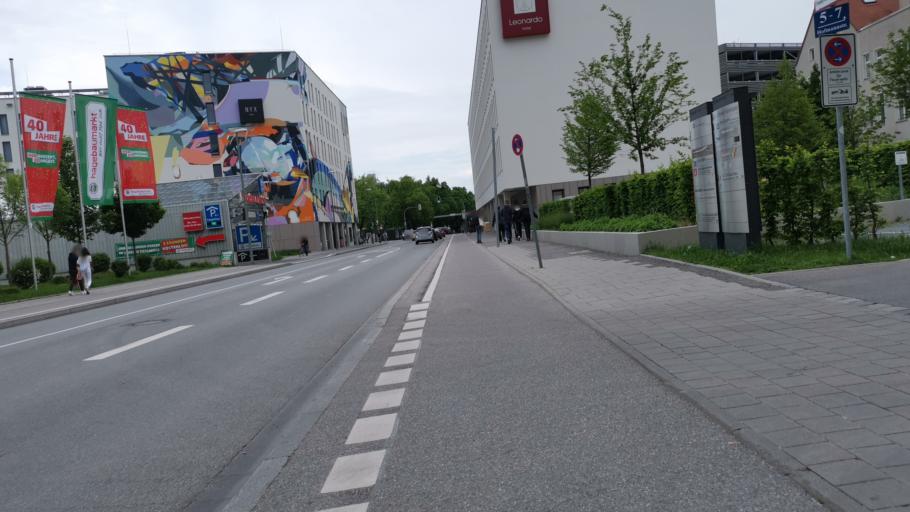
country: DE
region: Bavaria
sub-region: Upper Bavaria
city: Pullach im Isartal
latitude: 48.1015
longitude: 11.5297
